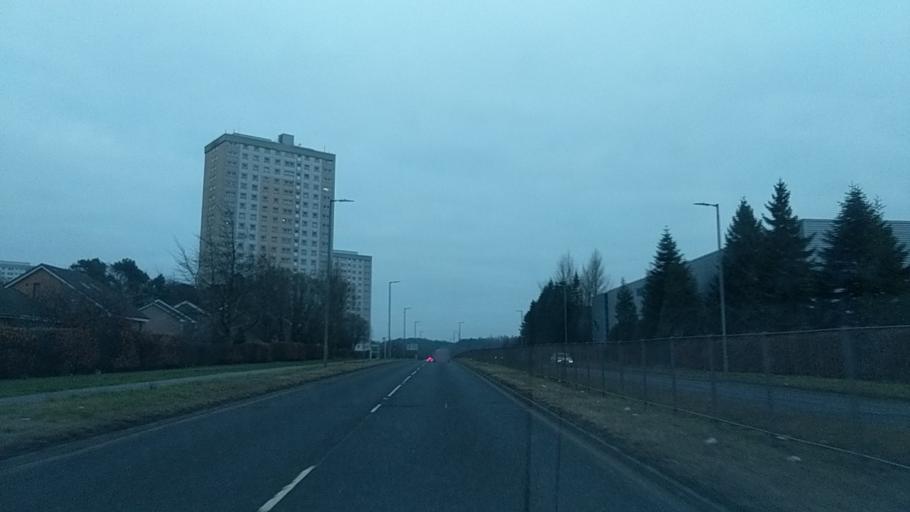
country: GB
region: Scotland
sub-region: South Lanarkshire
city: East Kilbride
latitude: 55.7561
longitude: -4.1614
